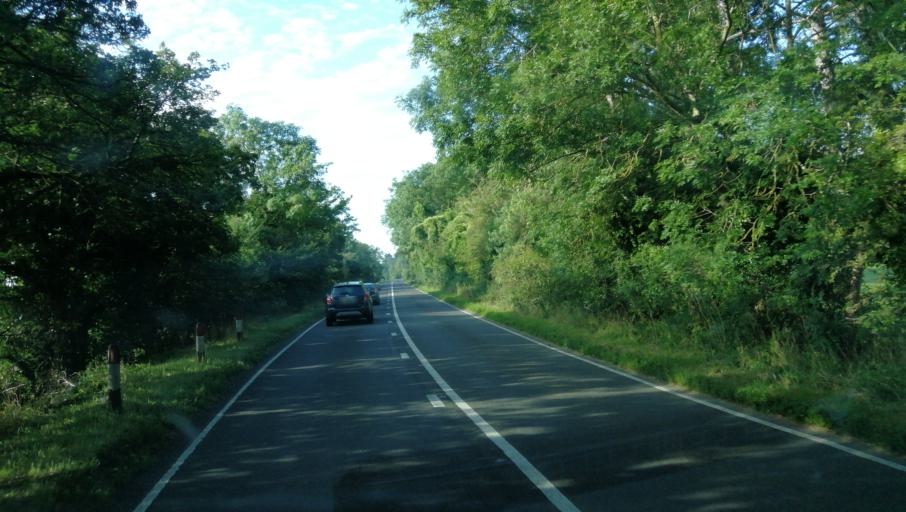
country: GB
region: England
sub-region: Oxfordshire
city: Somerton
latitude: 51.9166
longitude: -1.3253
